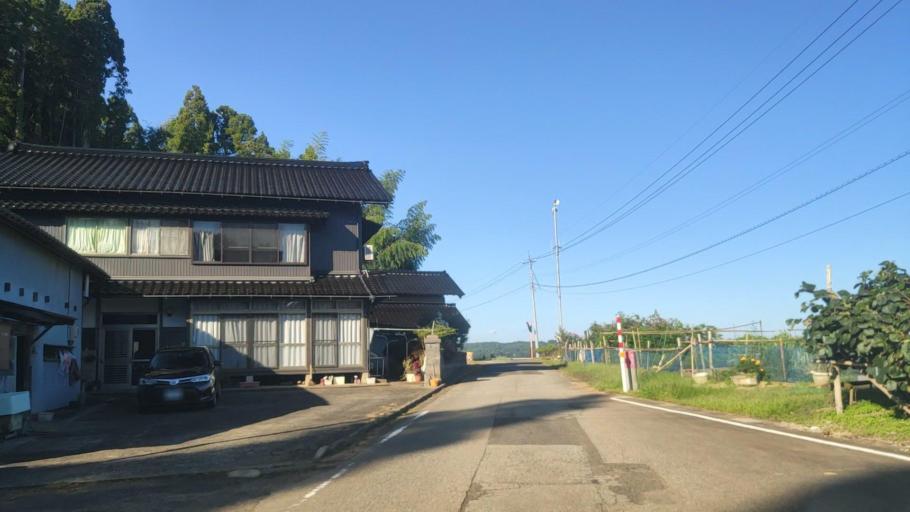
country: JP
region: Ishikawa
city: Nanao
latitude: 37.1209
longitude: 136.8941
